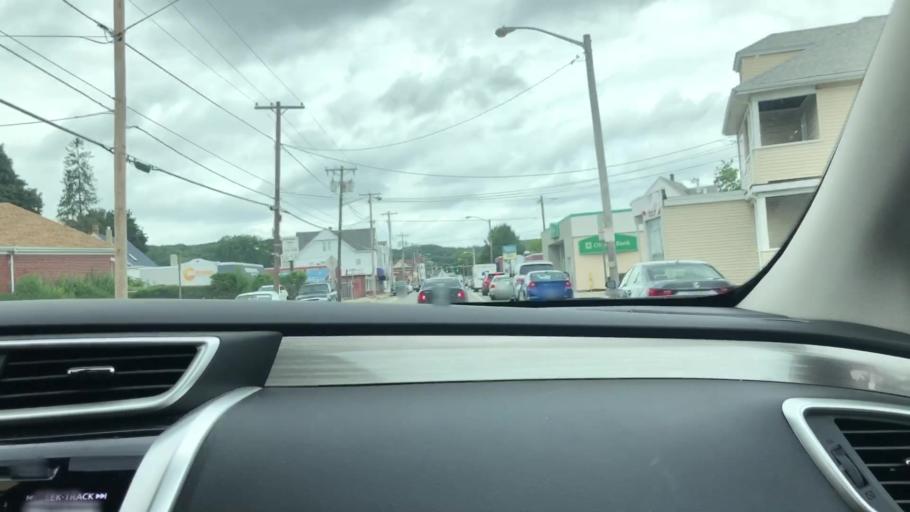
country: US
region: Rhode Island
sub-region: Providence County
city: Central Falls
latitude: 41.8765
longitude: -71.4148
